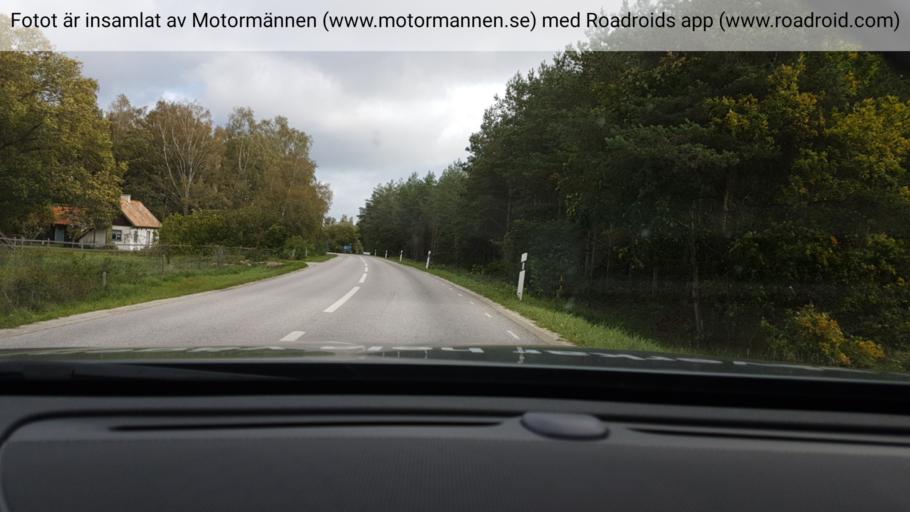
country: SE
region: Gotland
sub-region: Gotland
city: Visby
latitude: 57.6839
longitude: 18.4986
